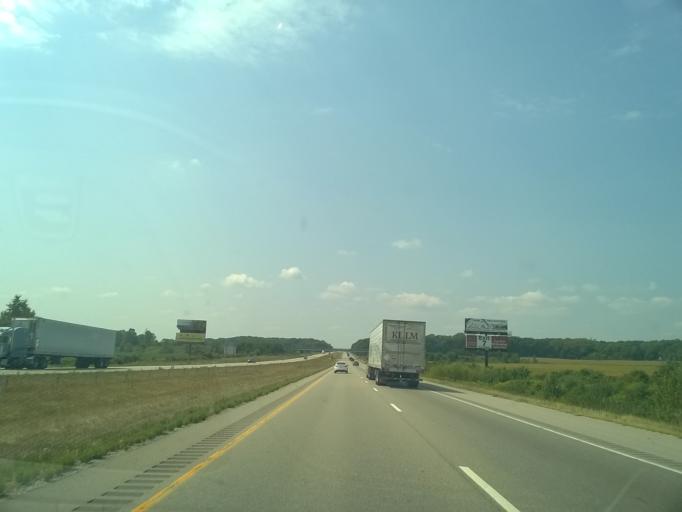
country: US
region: Indiana
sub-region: Clay County
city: Brazil
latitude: 39.4505
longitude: -87.1642
